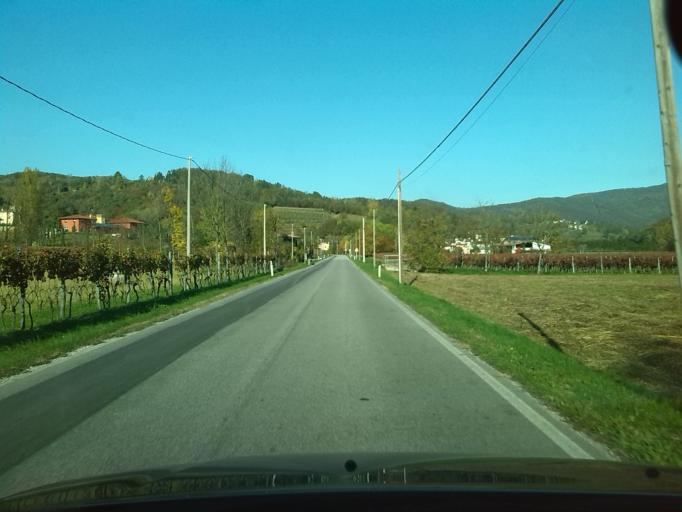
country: IT
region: Friuli Venezia Giulia
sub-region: Provincia di Udine
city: Prepotto
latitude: 46.0674
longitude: 13.4605
